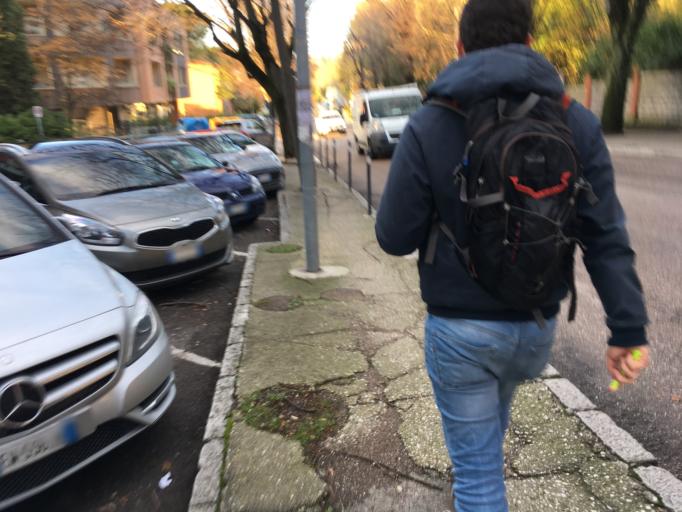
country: IT
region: Umbria
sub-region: Provincia di Perugia
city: Perugia
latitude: 43.1060
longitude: 12.3807
